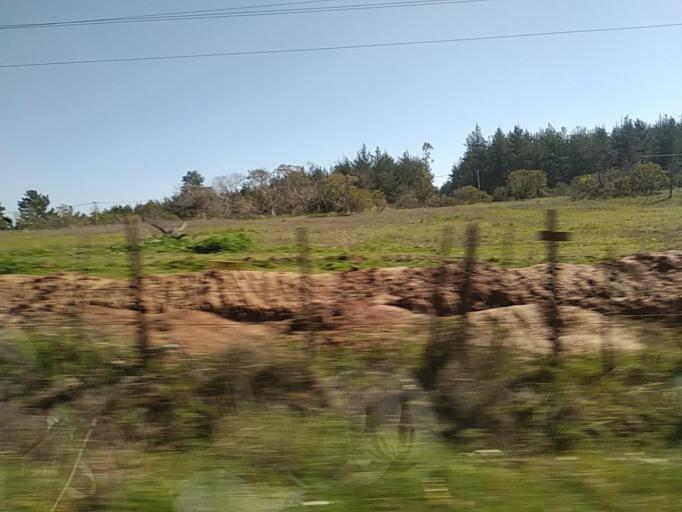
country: CL
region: Valparaiso
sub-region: San Antonio Province
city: El Tabo
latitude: -33.4027
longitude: -71.5892
